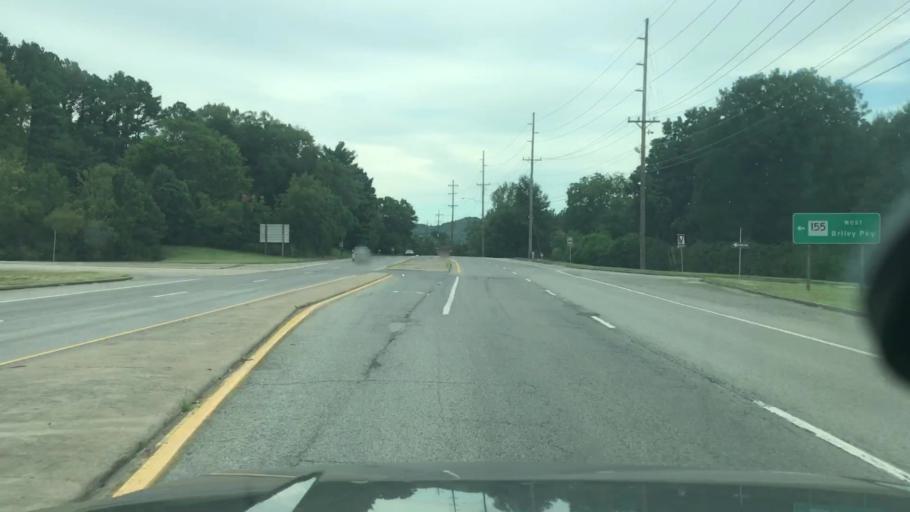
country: US
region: Tennessee
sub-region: Davidson County
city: Nashville
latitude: 36.2298
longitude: -86.8337
